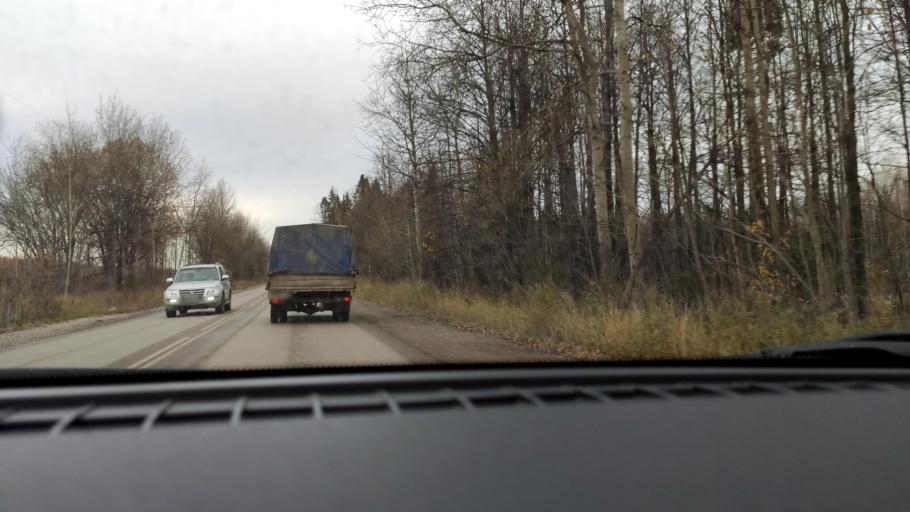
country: RU
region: Perm
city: Ferma
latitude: 57.9672
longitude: 56.3506
